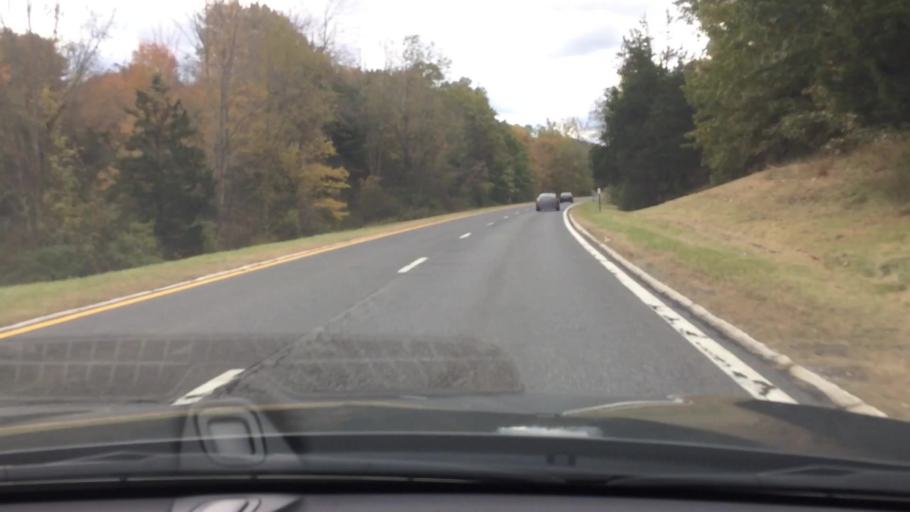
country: US
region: New York
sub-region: Dutchess County
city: Pleasant Valley
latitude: 41.7727
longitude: -73.7670
